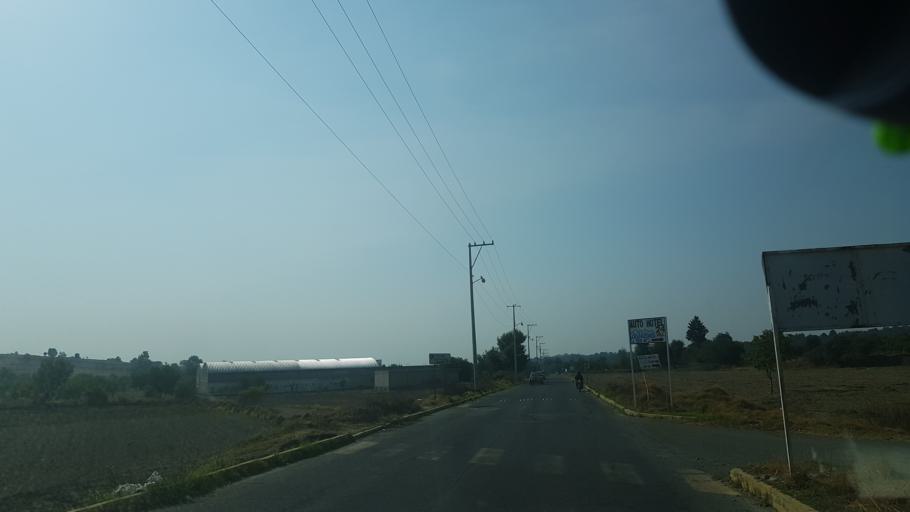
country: MX
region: Puebla
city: San Nicolas de los Ranchos
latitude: 19.0666
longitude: -98.4738
